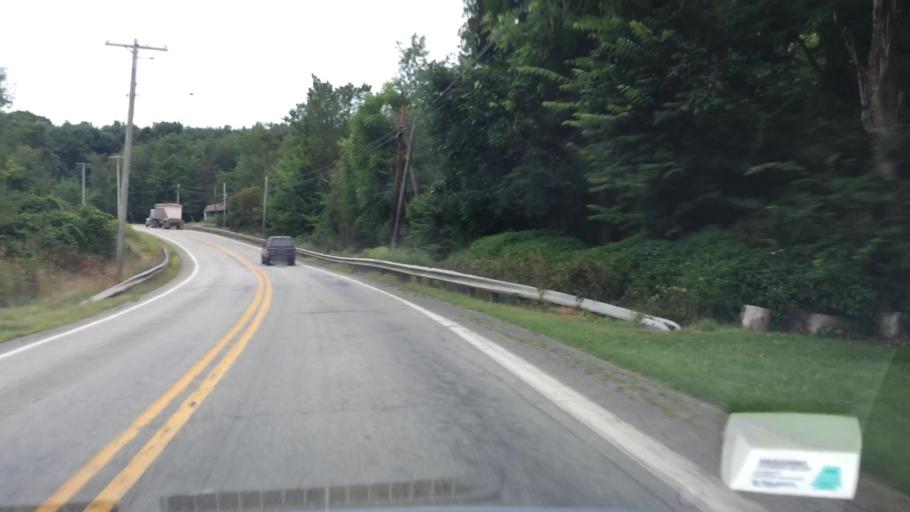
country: US
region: Pennsylvania
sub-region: Allegheny County
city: Curtisville
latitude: 40.6661
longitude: -79.8351
